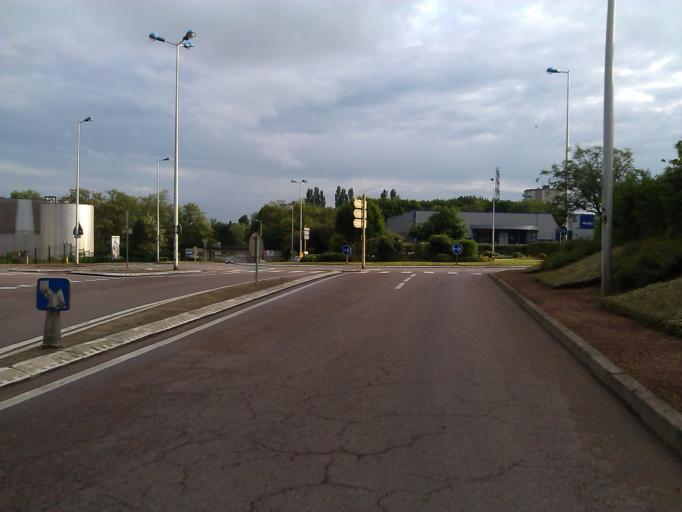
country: FR
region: Bourgogne
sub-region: Departement de Saone-et-Loire
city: Crissey
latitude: 46.8069
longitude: 4.8621
